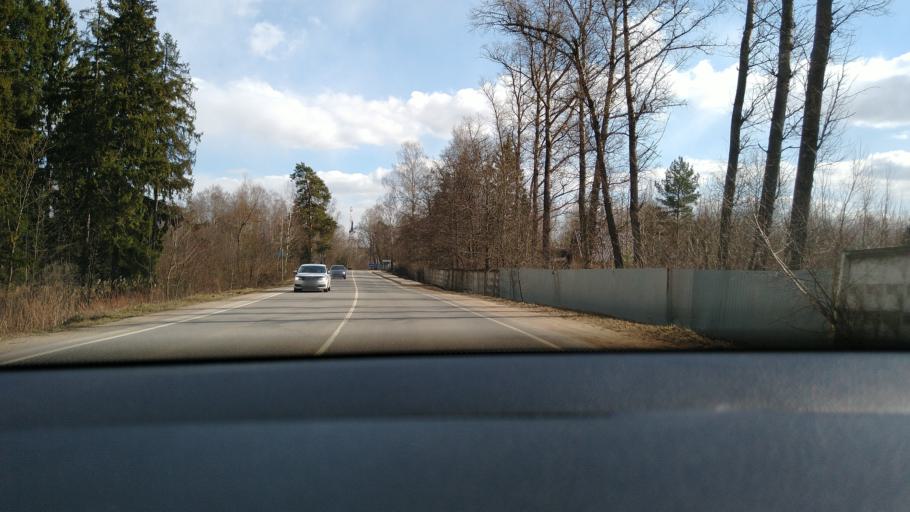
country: RU
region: Moskovskaya
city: Zvenigorod
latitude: 55.6473
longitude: 36.8231
